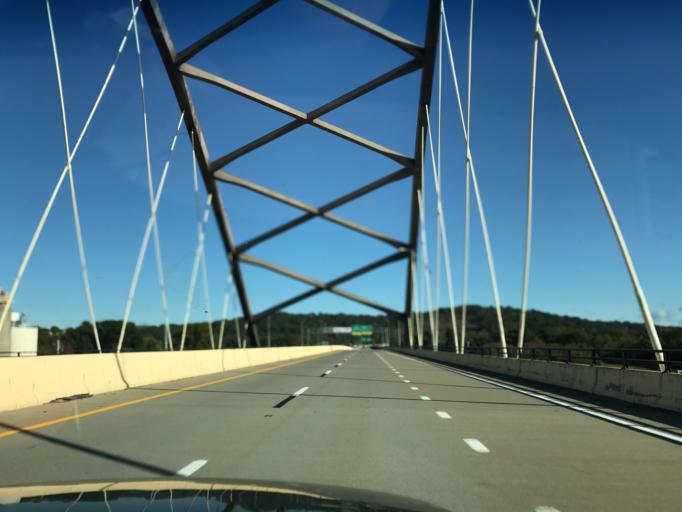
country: US
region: West Virginia
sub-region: Wood County
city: Blennerhassett
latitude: 39.2764
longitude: -81.6468
